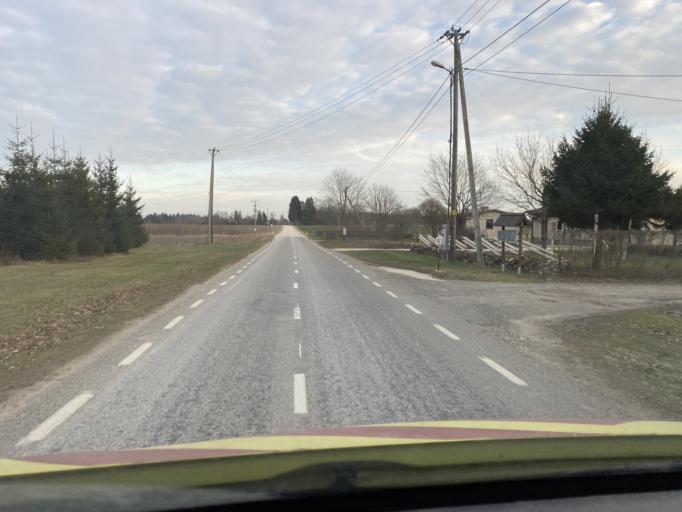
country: EE
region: Jogevamaa
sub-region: Poltsamaa linn
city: Poltsamaa
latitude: 58.5948
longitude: 26.0079
